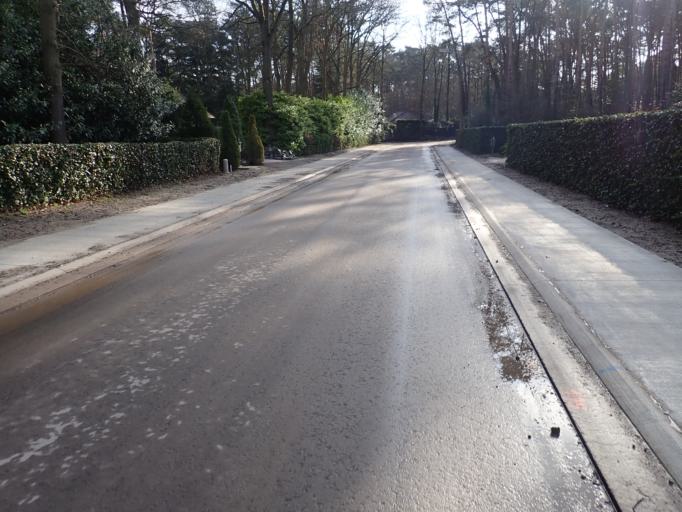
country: BE
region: Flanders
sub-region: Provincie Vlaams-Brabant
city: Keerbergen
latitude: 51.0071
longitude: 4.6495
